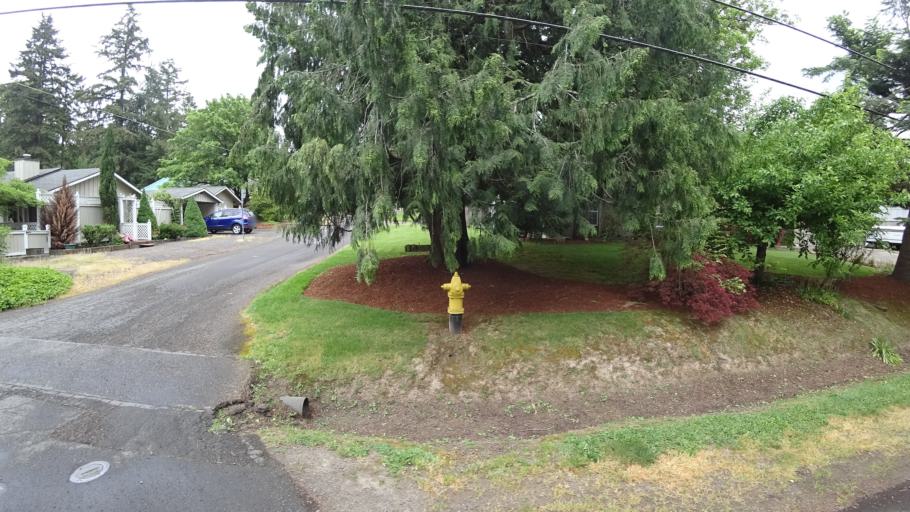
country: US
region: Oregon
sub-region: Washington County
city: Garden Home-Whitford
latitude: 45.4635
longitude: -122.7659
